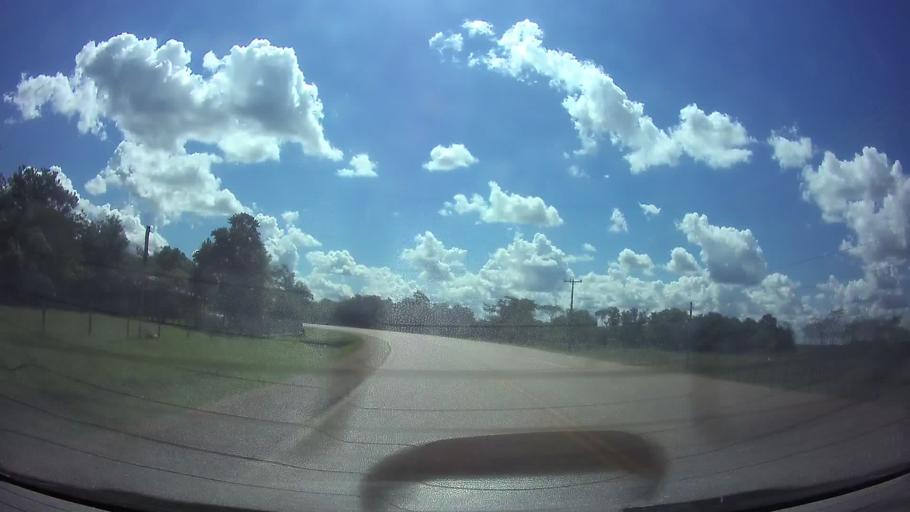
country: PY
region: Guaira
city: Itape
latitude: -25.9144
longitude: -56.6968
